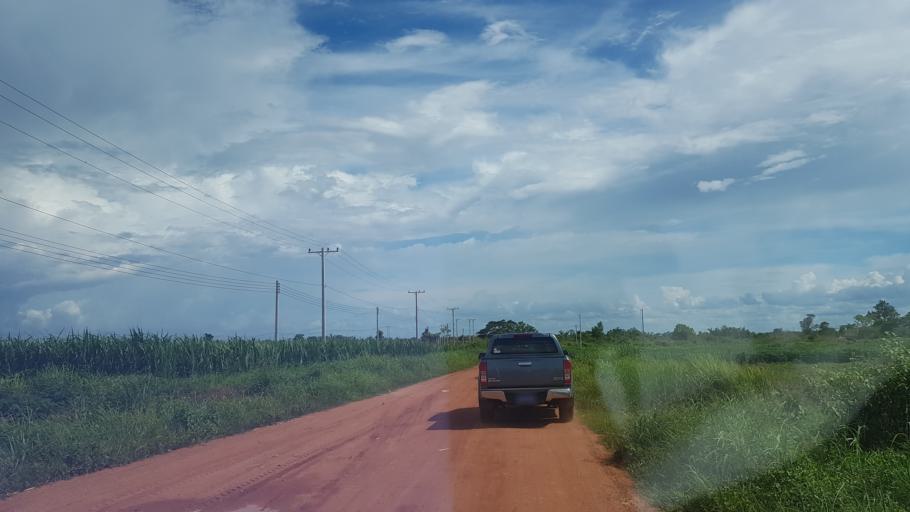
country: LA
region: Vientiane
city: Vientiane
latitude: 18.2118
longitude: 102.5661
